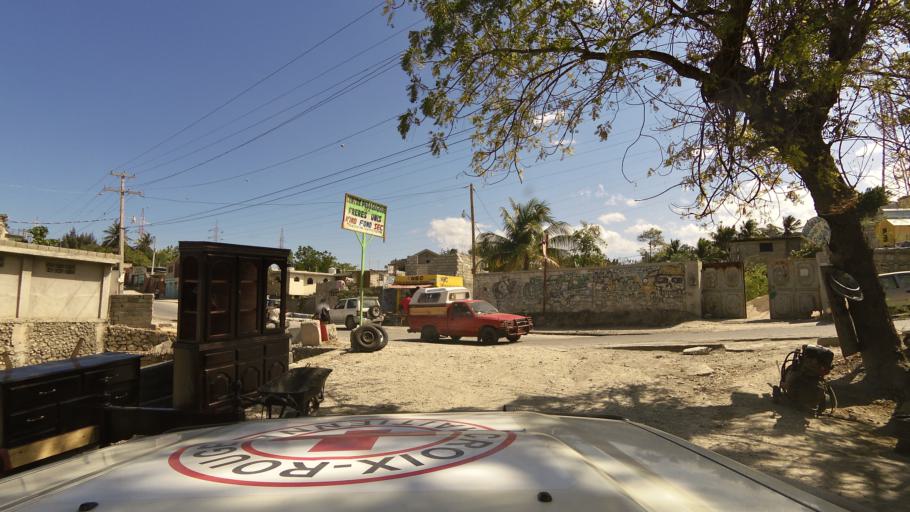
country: HT
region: Ouest
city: Delmas 73
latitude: 18.5597
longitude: -72.2953
